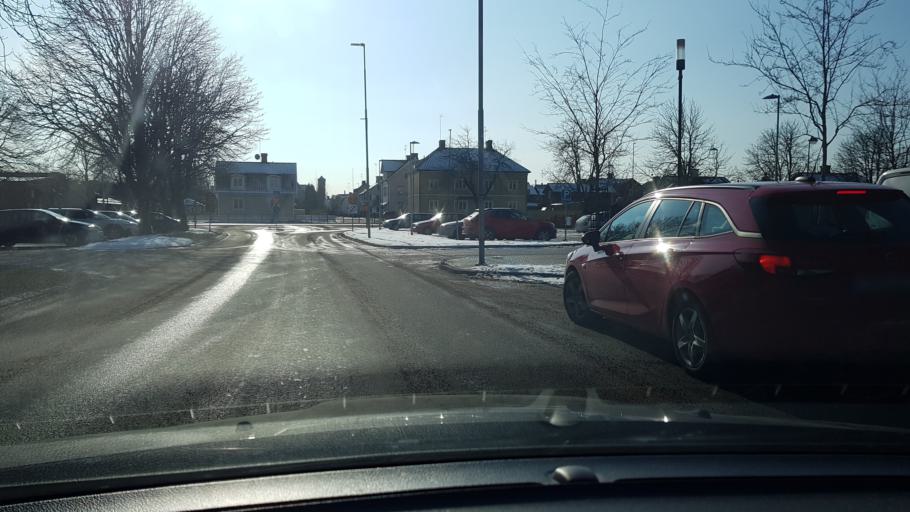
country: SE
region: Vaestmanland
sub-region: Sala Kommun
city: Sala
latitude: 59.9204
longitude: 16.5997
